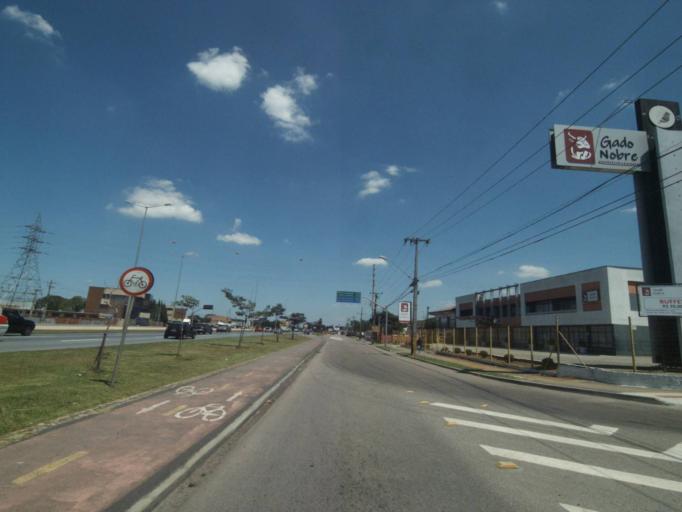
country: BR
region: Parana
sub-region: Sao Jose Dos Pinhais
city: Sao Jose dos Pinhais
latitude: -25.5240
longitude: -49.2964
